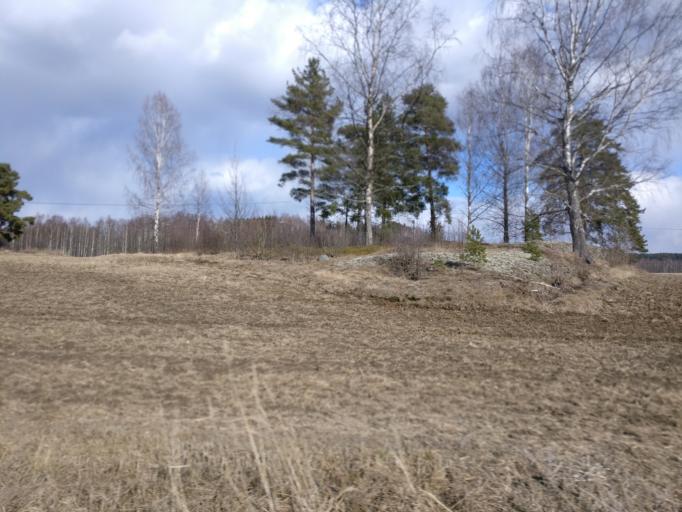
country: FI
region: Uusimaa
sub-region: Helsinki
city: Karjalohja
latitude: 60.3059
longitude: 23.7479
